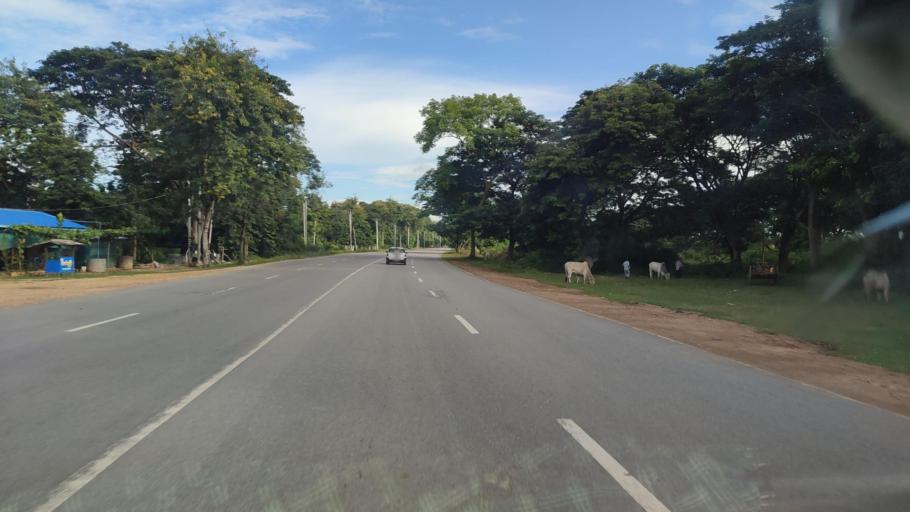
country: MM
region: Mandalay
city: Yamethin
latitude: 20.1922
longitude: 96.1843
